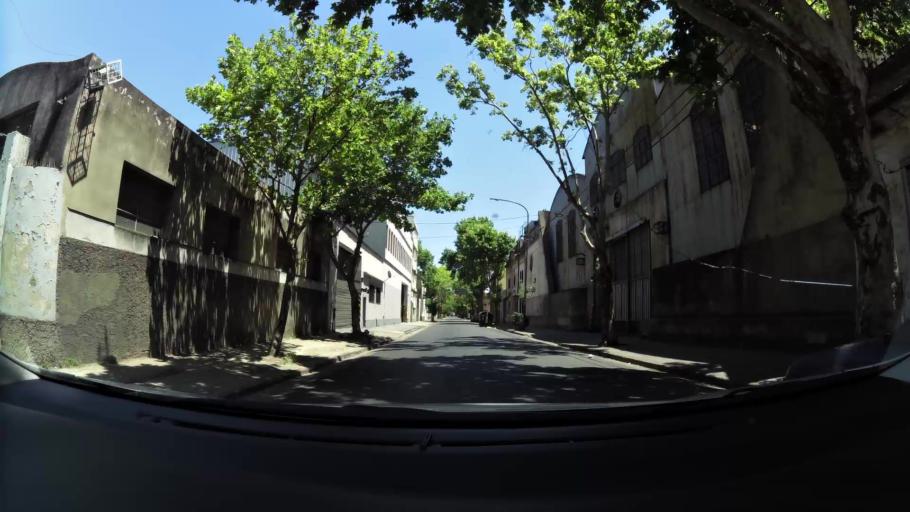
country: AR
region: Buenos Aires
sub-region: Partido de Avellaneda
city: Avellaneda
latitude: -34.6535
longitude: -58.3801
